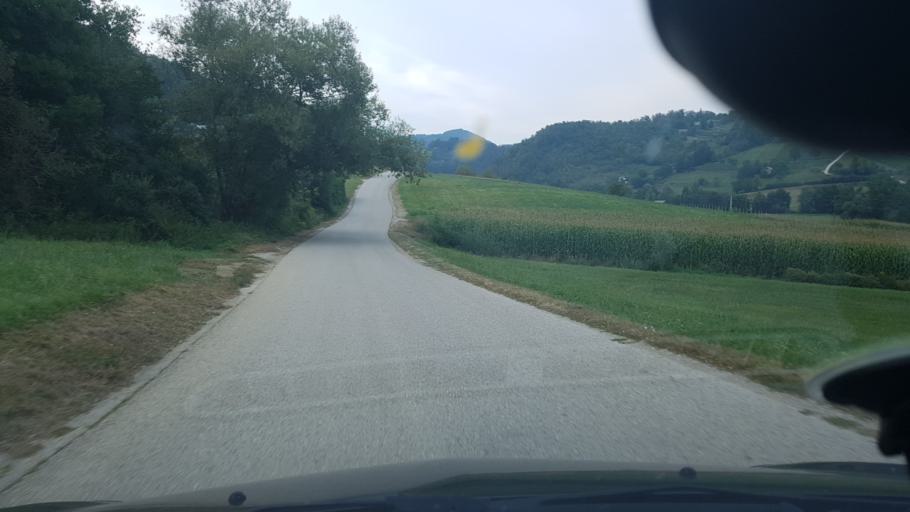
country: SI
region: Krsko
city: Senovo
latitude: 46.0335
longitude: 15.5155
